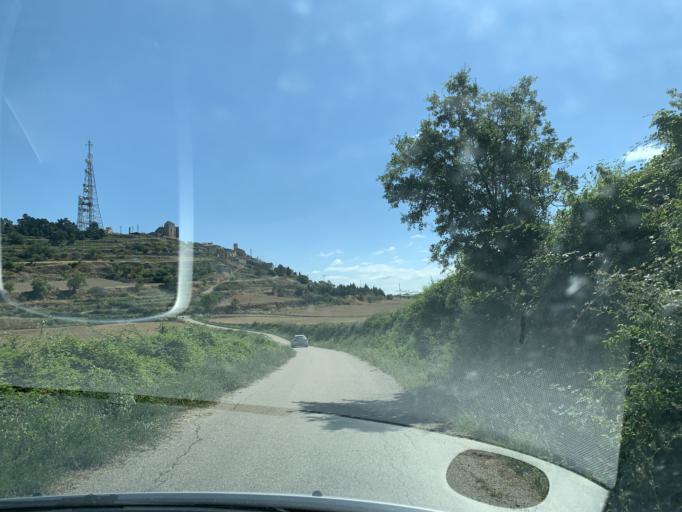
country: ES
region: Catalonia
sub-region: Provincia de Tarragona
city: Conesa
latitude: 41.5412
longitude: 1.2936
